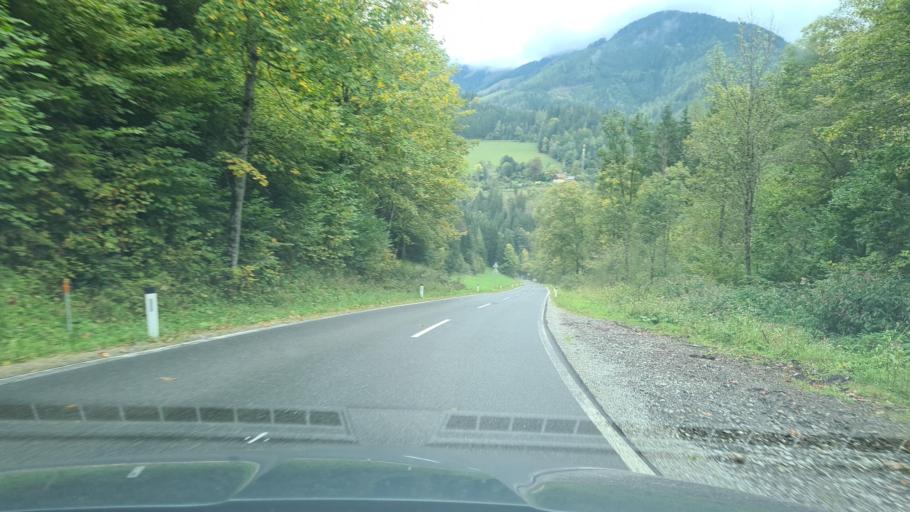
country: AT
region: Styria
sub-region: Politischer Bezirk Weiz
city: Gasen
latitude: 47.3768
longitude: 15.4874
